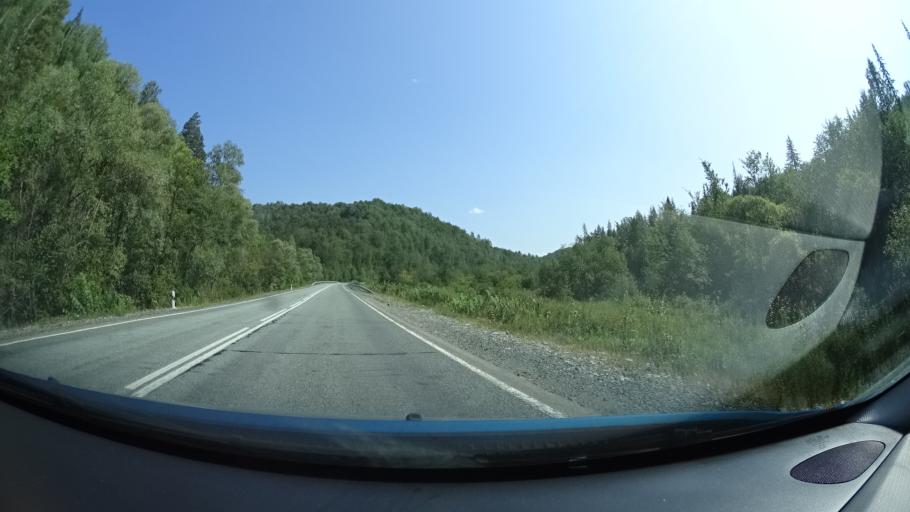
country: RU
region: Bashkortostan
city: Inzer
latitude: 54.3179
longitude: 57.1807
